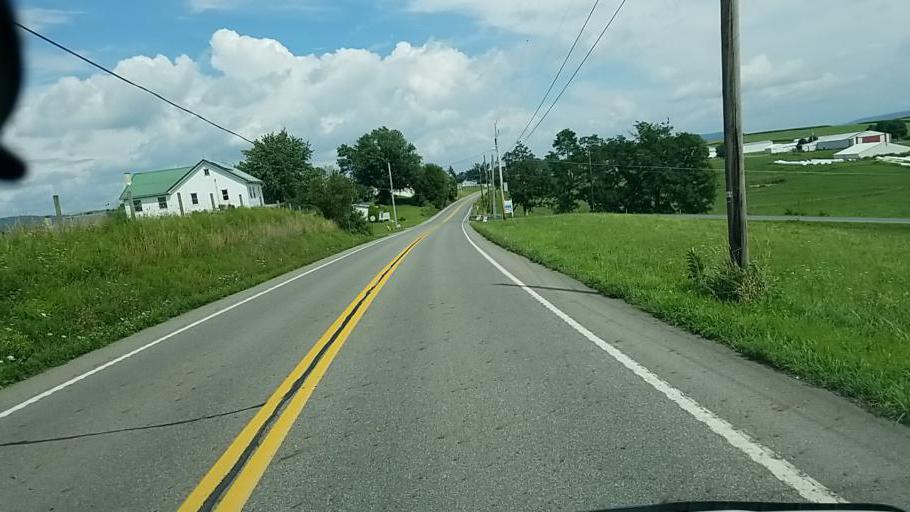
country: US
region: Pennsylvania
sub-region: Dauphin County
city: Elizabethville
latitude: 40.5809
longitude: -76.8778
